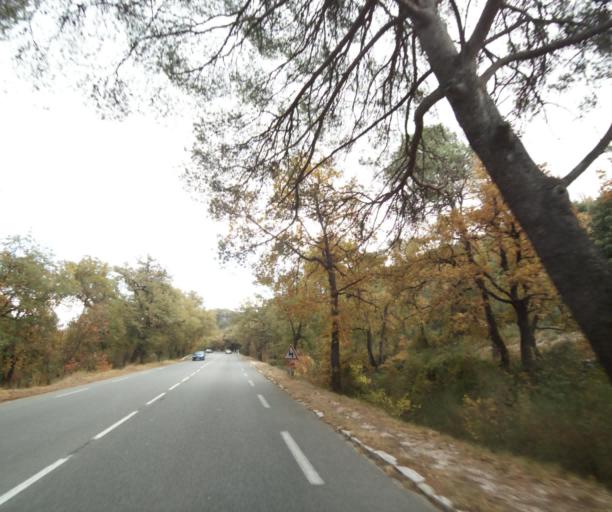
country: FR
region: Provence-Alpes-Cote d'Azur
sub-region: Departement des Bouches-du-Rhone
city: Cuges-les-Pins
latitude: 43.2653
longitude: 5.6639
